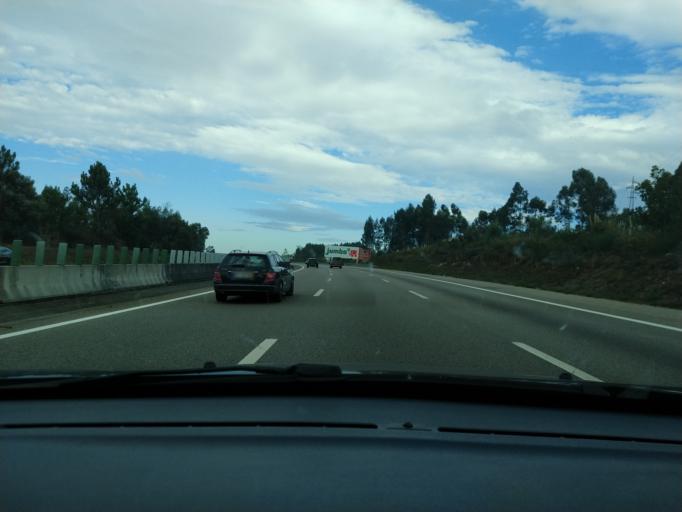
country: PT
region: Aveiro
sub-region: Santa Maria da Feira
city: Rio Meao
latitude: 40.9654
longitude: -8.5678
